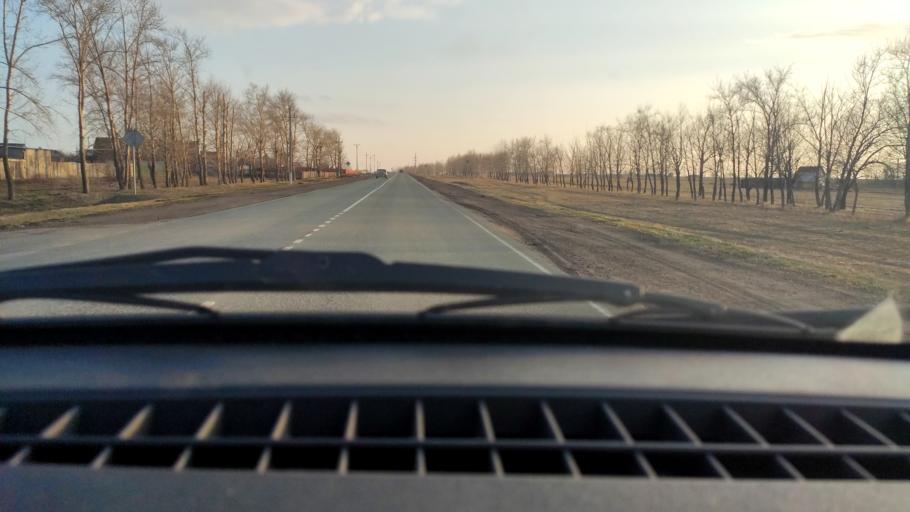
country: RU
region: Bashkortostan
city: Davlekanovo
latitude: 54.3897
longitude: 55.2019
